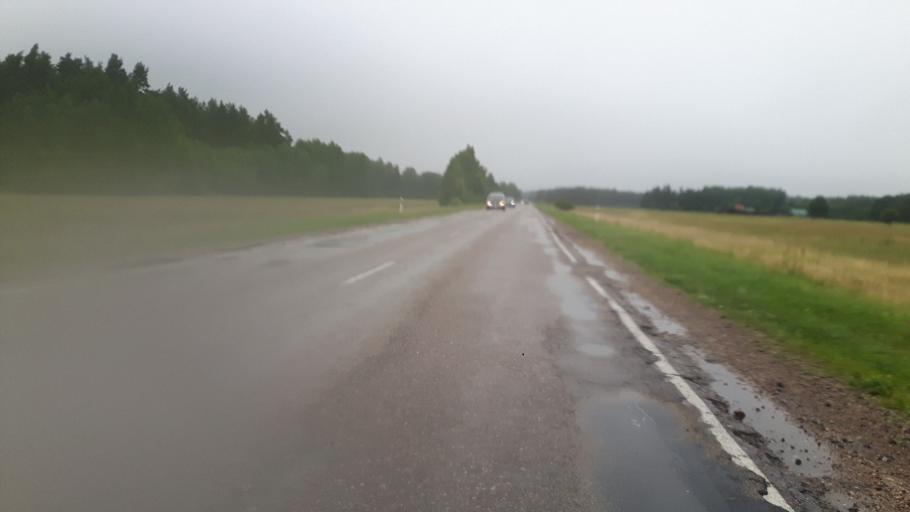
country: LV
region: Rucavas
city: Rucava
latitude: 56.0982
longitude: 21.1318
